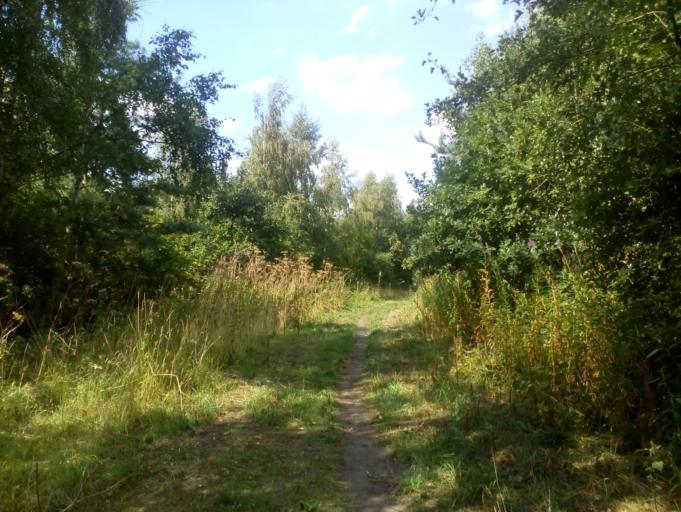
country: GB
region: England
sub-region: North Yorkshire
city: Hambleton
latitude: 53.7639
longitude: -1.1396
